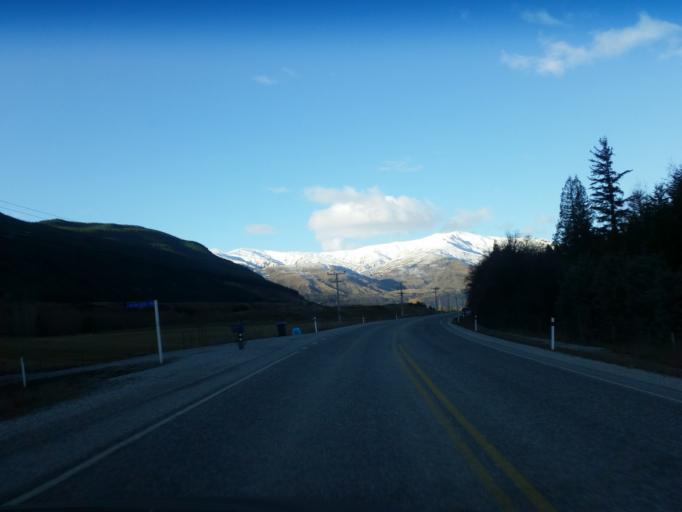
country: NZ
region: Otago
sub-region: Queenstown-Lakes District
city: Arrowtown
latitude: -44.9463
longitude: 168.7699
